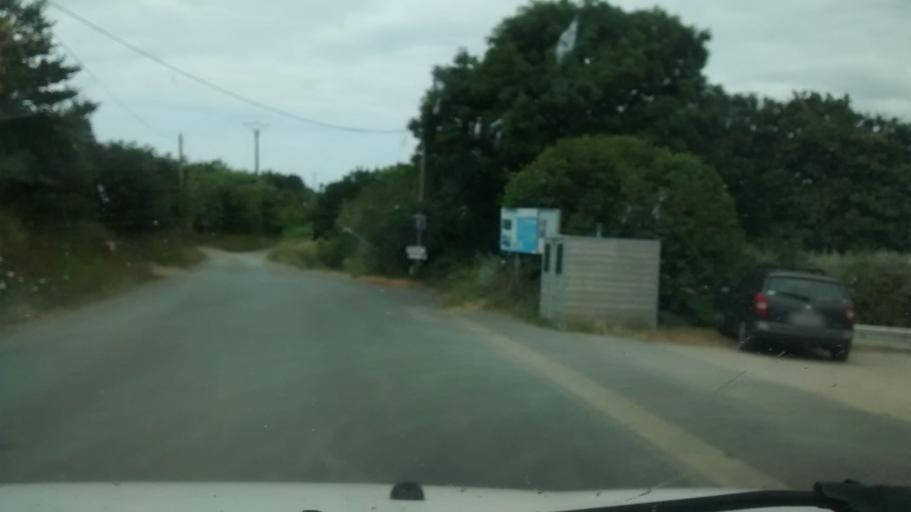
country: FR
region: Brittany
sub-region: Departement du Finistere
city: Lanveoc
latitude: 48.3284
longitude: -4.4480
